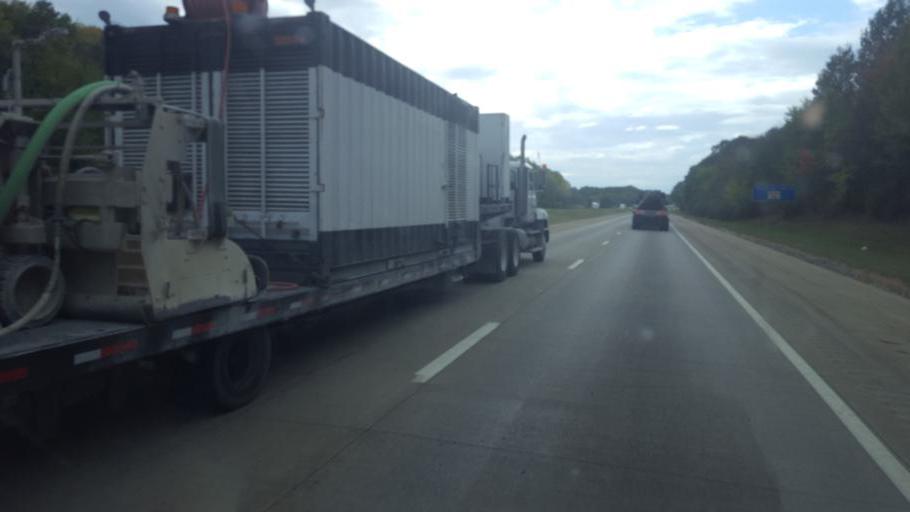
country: US
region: Ohio
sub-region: Mahoning County
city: Craig Beach
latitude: 41.1049
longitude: -80.9269
